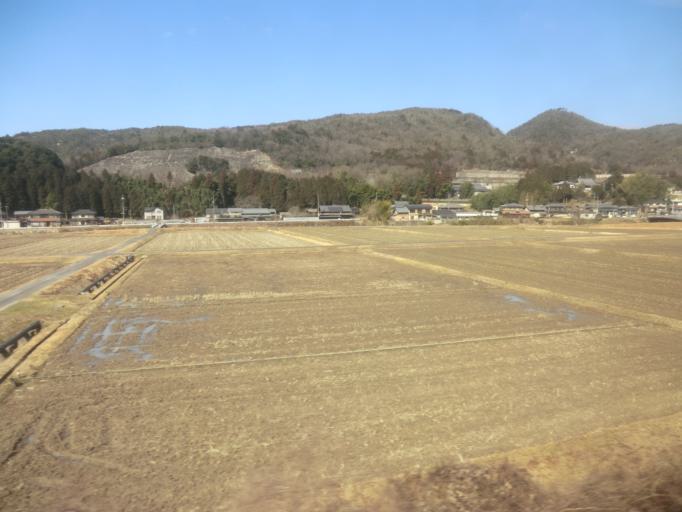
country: JP
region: Gifu
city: Mizunami
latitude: 35.4029
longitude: 137.2979
